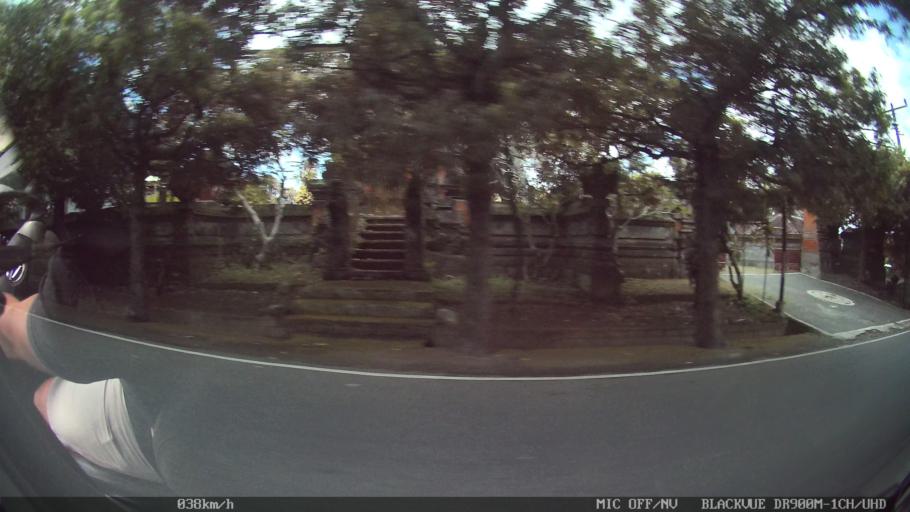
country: ID
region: Bali
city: Banjar Sedang
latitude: -8.5636
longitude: 115.2769
